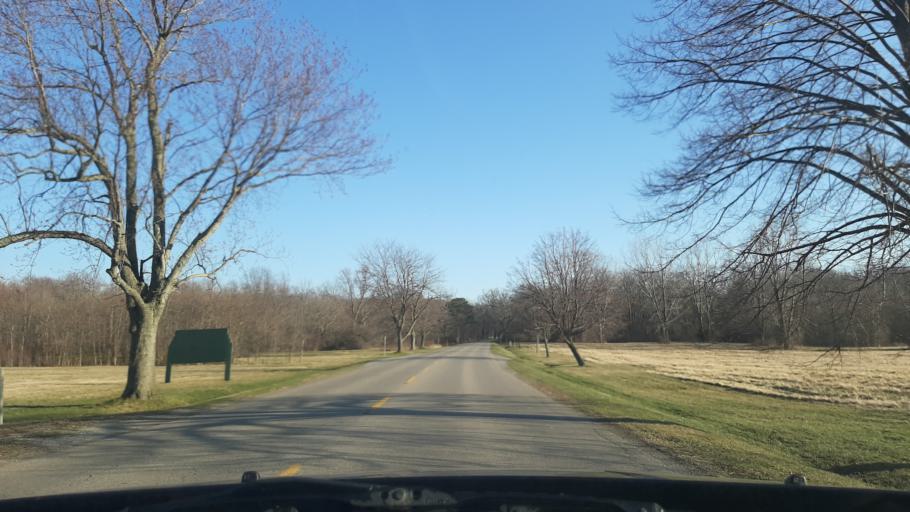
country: US
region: New York
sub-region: Niagara County
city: Youngstown
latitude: 43.2478
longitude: -79.0639
